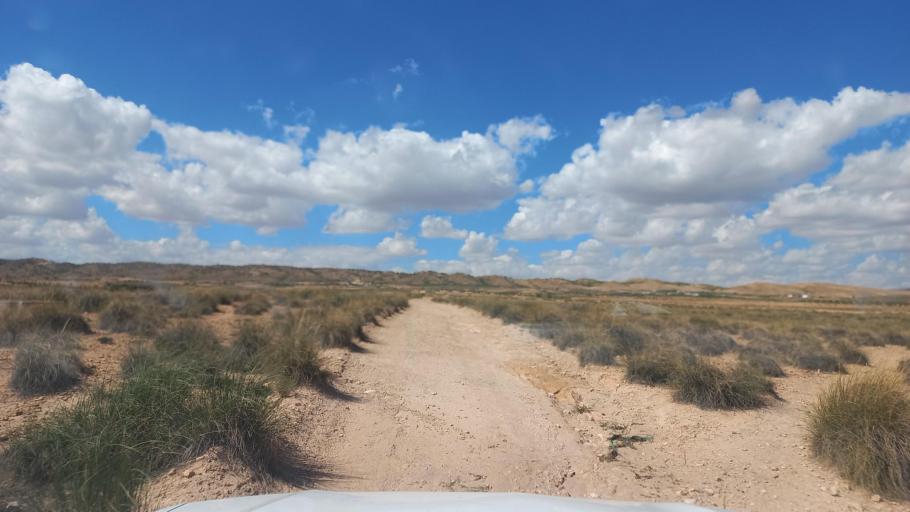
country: TN
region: Al Qasrayn
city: Sbiba
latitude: 35.3565
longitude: 9.0100
